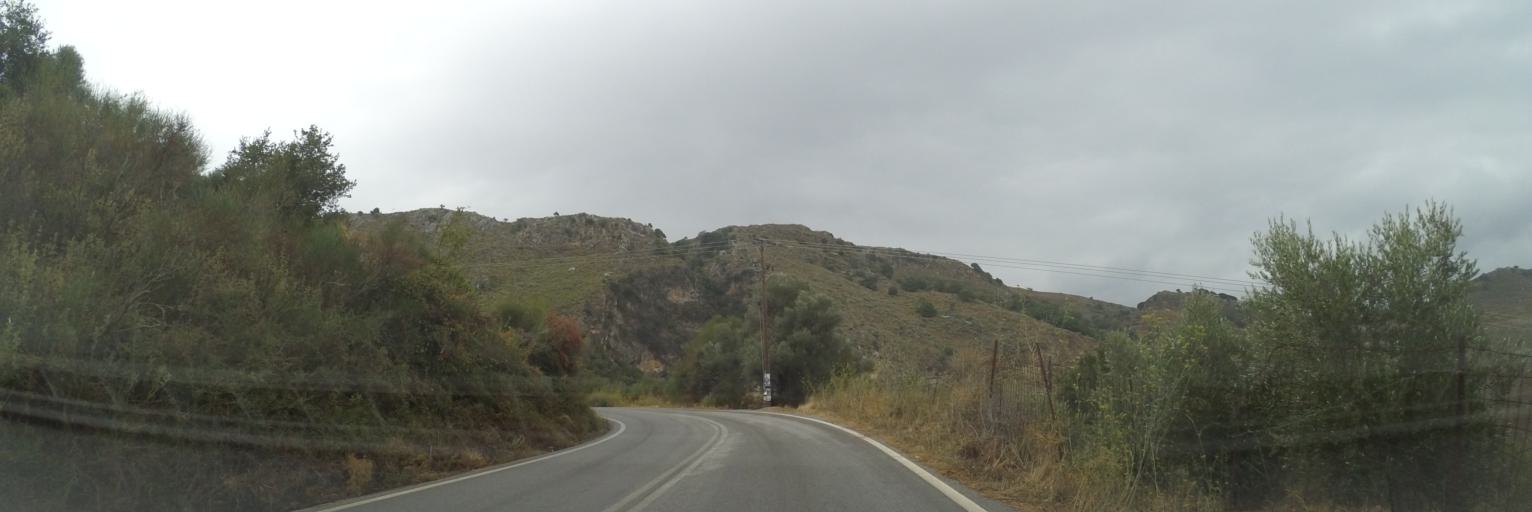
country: GR
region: Crete
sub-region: Nomos Rethymnis
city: Agia Foteini
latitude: 35.2928
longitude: 24.5641
